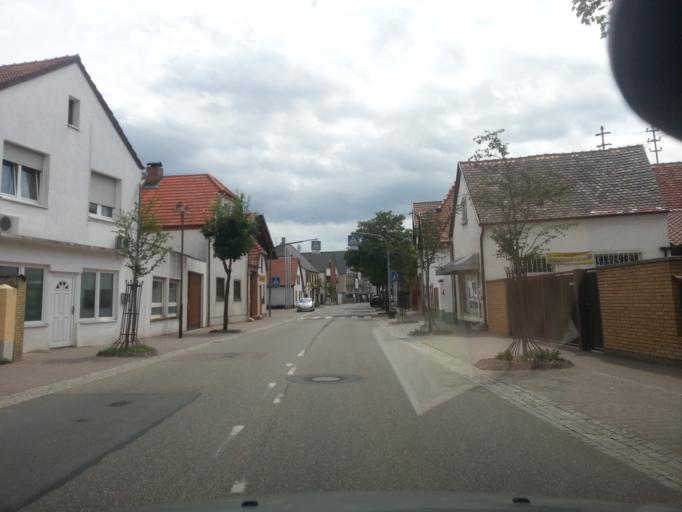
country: DE
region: Rheinland-Pfalz
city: Hessheim
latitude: 49.5474
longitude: 8.3086
